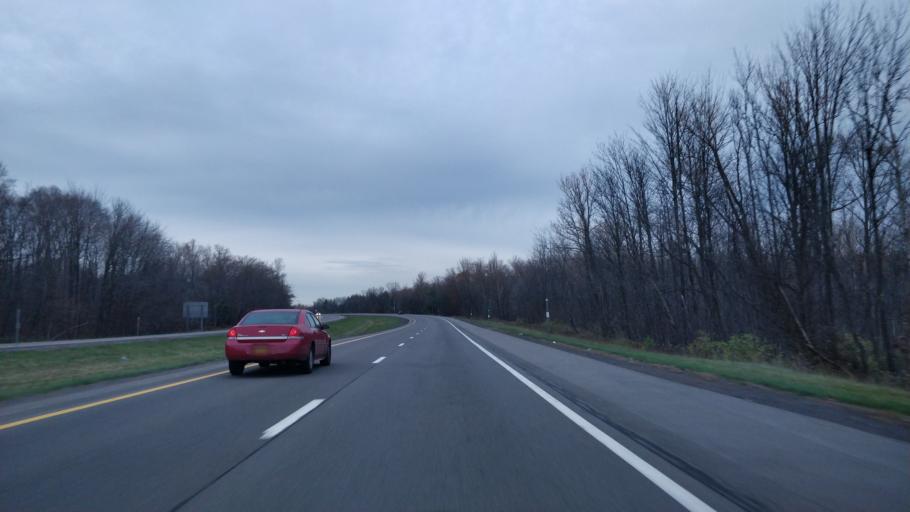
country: US
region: New York
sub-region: Oswego County
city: Central Square
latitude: 43.2968
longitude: -76.1245
